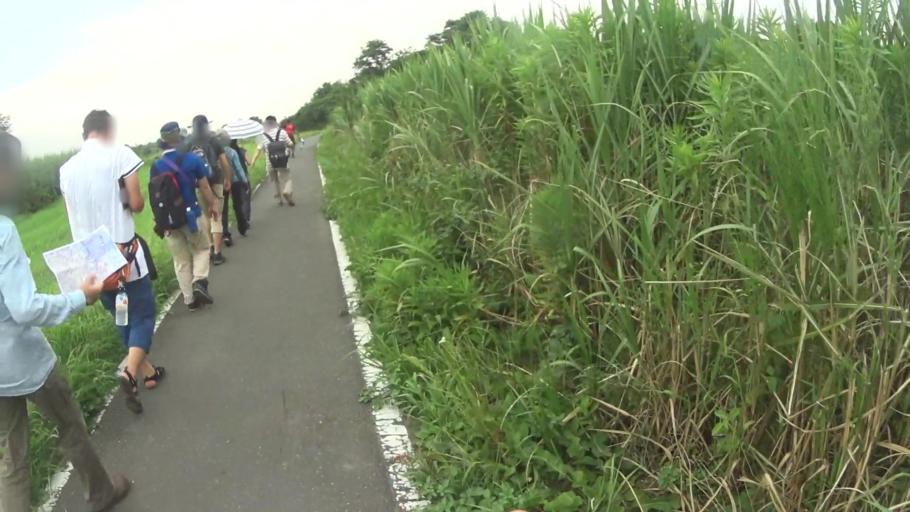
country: JP
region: Saitama
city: Okegawa
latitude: 35.9550
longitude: 139.5437
